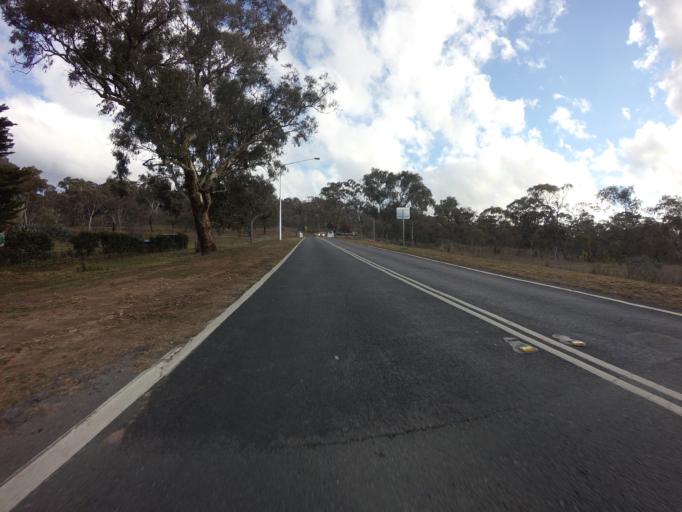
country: AU
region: Australian Capital Territory
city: Forrest
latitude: -35.3198
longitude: 149.1141
